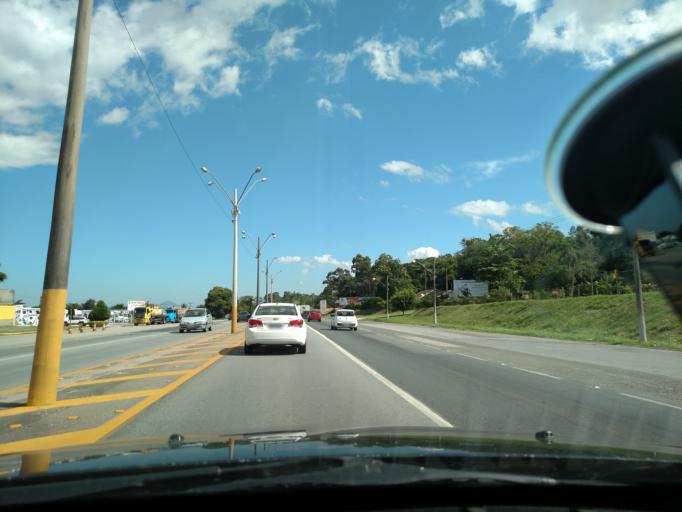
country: BR
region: Santa Catarina
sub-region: Biguacu
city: Biguacu
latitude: -27.4700
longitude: -48.6414
